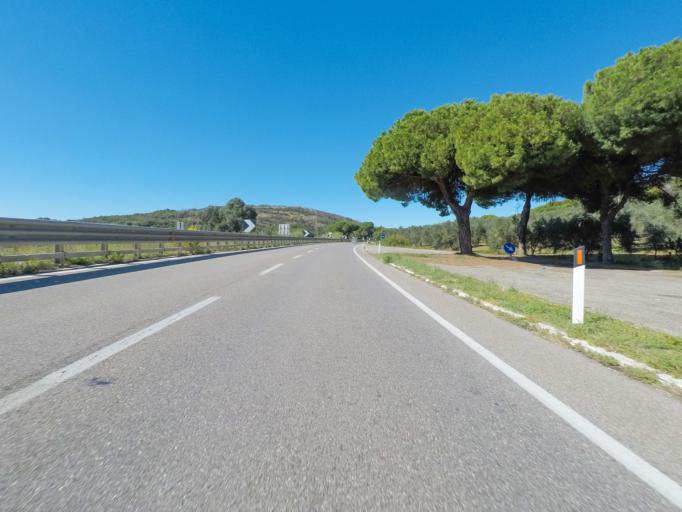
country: IT
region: Tuscany
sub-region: Provincia di Grosseto
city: Orbetello Scalo
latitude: 42.4206
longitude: 11.2908
